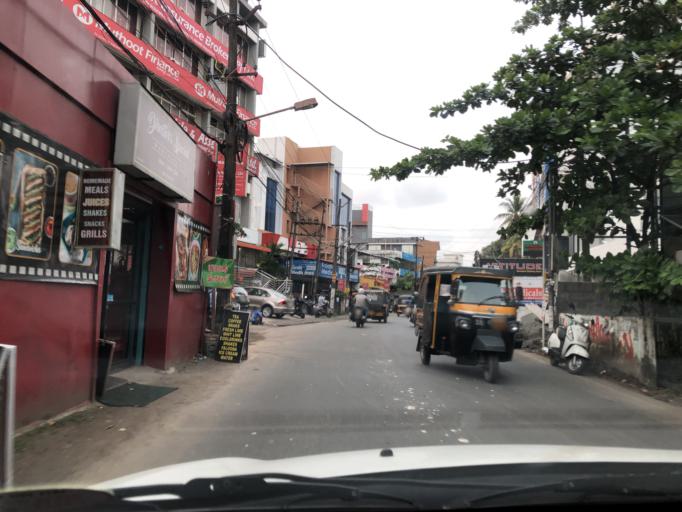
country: IN
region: Kerala
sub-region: Ernakulam
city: Cochin
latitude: 9.9621
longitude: 76.3010
